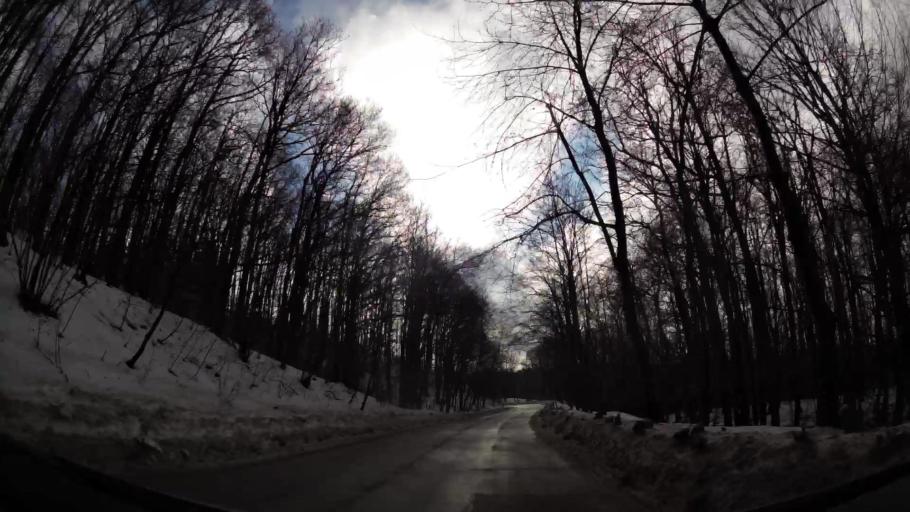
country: BG
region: Sofiya
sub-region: Obshtina Bozhurishte
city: Bozhurishte
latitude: 42.6395
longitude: 23.2170
